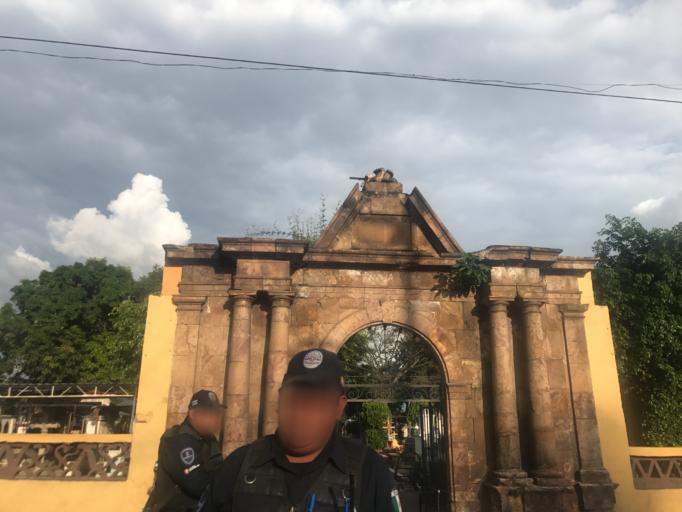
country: MX
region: Morelos
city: Jonacatepec de Leandro Valle
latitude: 18.6747
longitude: -98.8046
